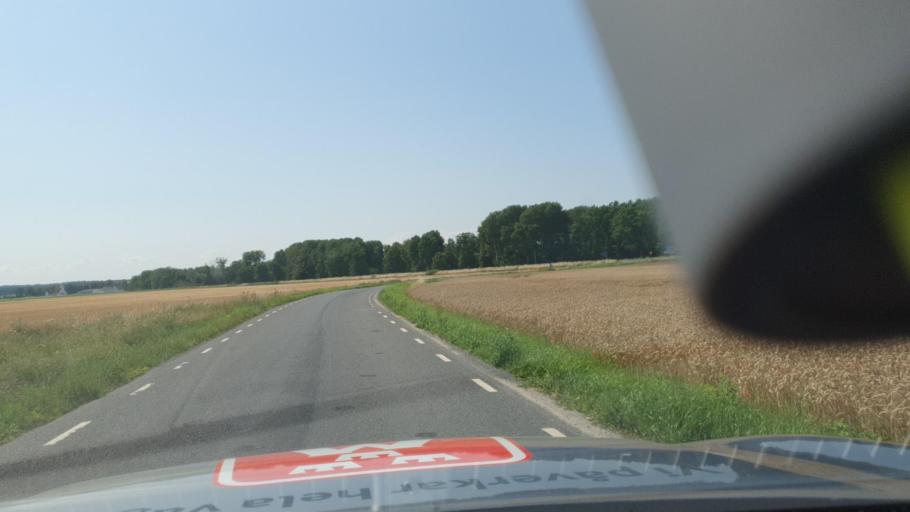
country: SE
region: Skane
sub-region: Kristianstads Kommun
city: Fjalkinge
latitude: 56.0731
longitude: 14.3481
